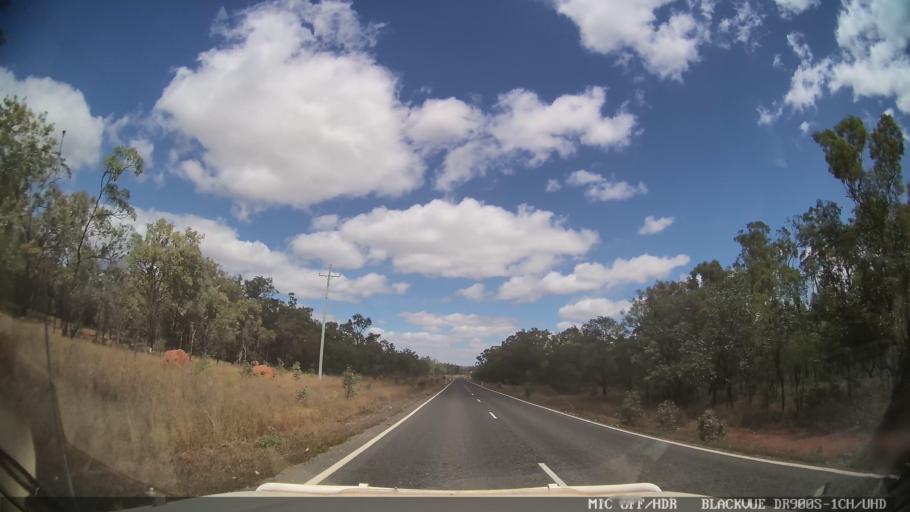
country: AU
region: Queensland
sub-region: Tablelands
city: Ravenshoe
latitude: -18.0290
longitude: 144.8700
